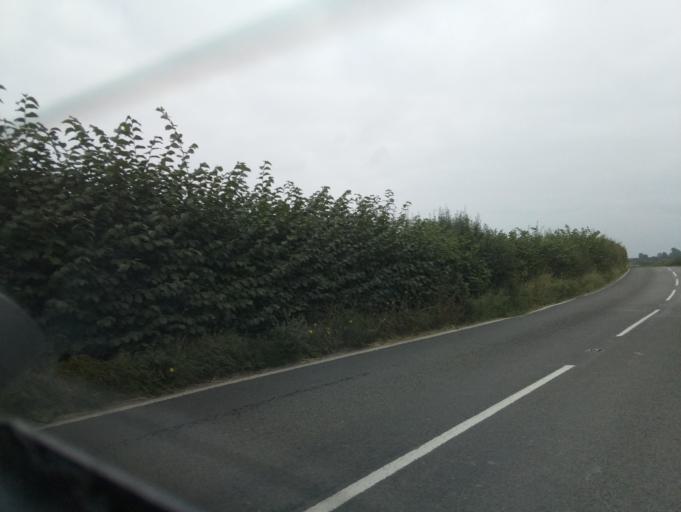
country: GB
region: England
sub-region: Derbyshire
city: Duffield
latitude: 53.0158
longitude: -1.5408
